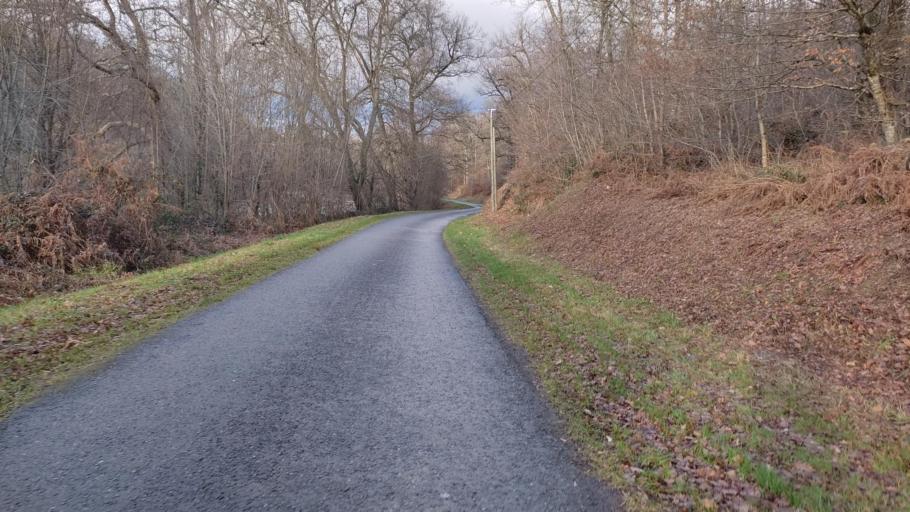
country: FR
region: Limousin
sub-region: Departement de la Haute-Vienne
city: Saint-Priest-sous-Aixe
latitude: 45.8147
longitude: 1.1194
